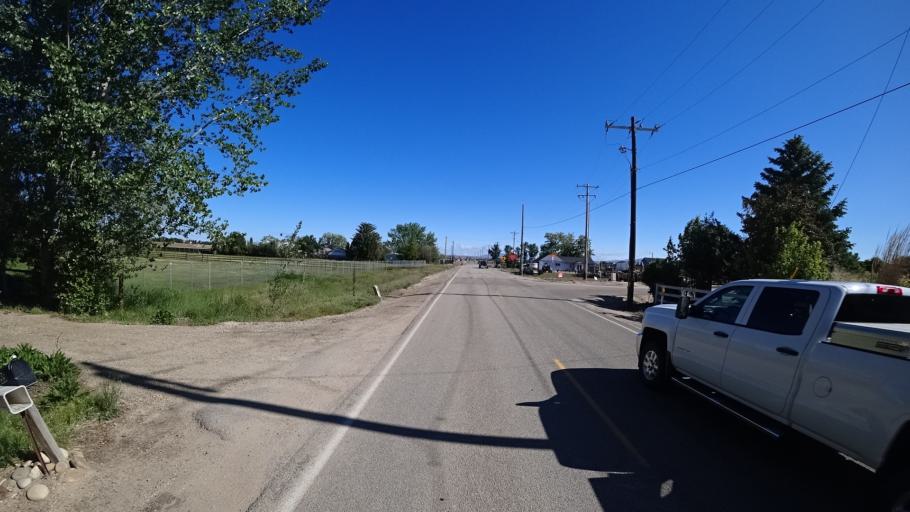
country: US
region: Idaho
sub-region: Ada County
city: Star
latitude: 43.6608
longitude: -116.4537
